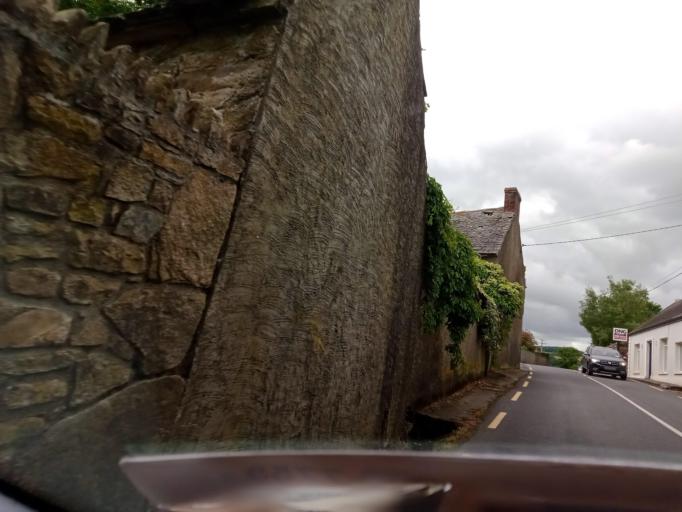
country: IE
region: Leinster
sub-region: Kilkenny
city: Thomastown
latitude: 52.4713
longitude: -7.2631
